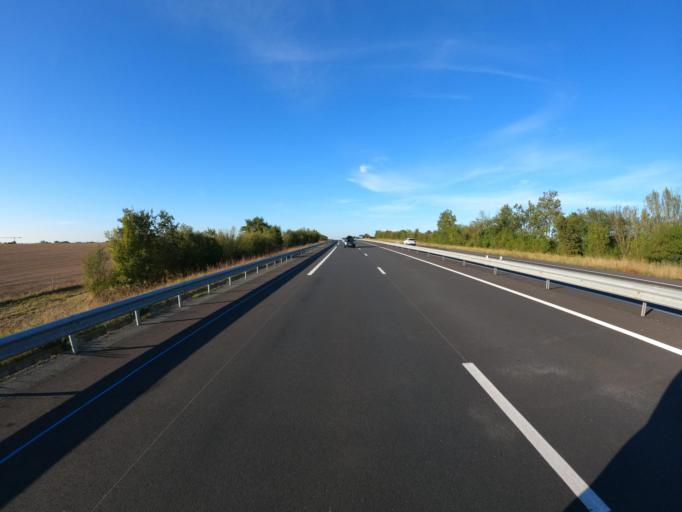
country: FR
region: Pays de la Loire
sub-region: Departement de la Vendee
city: Saint-Laurent-sur-Sevre
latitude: 46.9743
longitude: -0.9177
